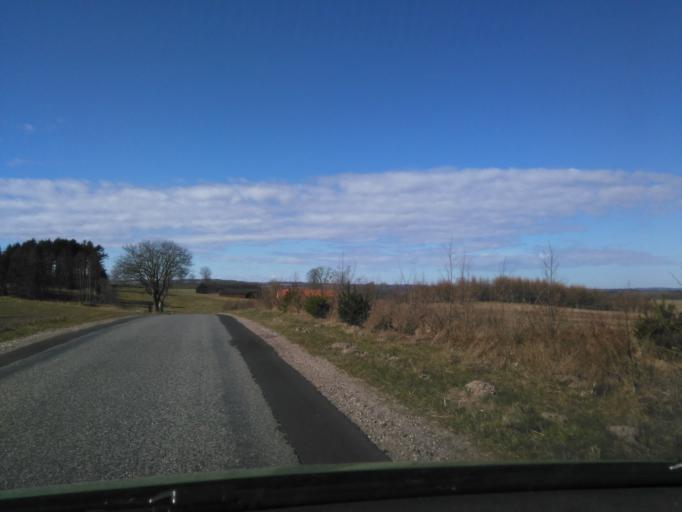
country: DK
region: Central Jutland
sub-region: Skanderborg Kommune
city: Stilling
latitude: 55.9723
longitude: 10.0195
